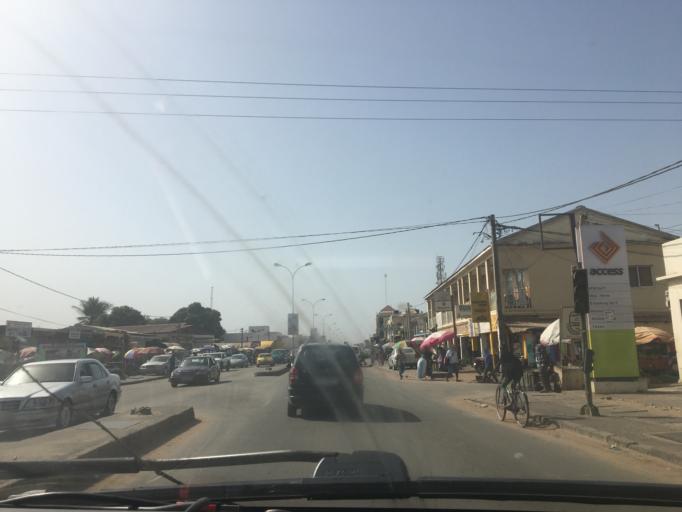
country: GM
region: Western
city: Abuko
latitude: 13.4128
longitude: -16.6711
